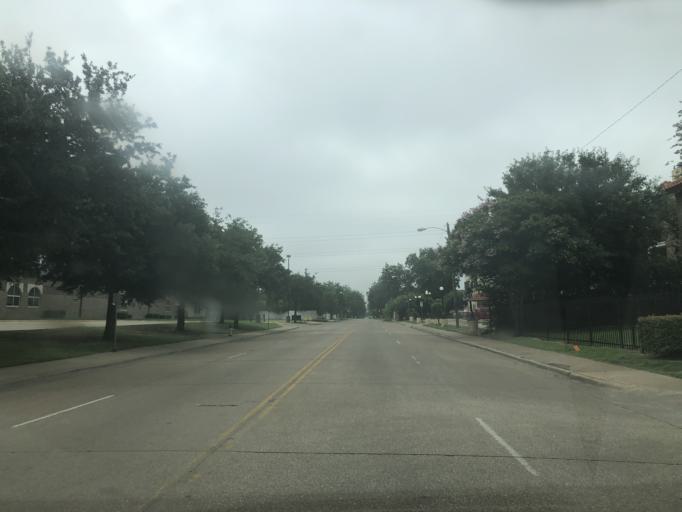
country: US
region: Texas
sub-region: Dallas County
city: Farmers Branch
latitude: 32.8646
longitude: -96.8741
